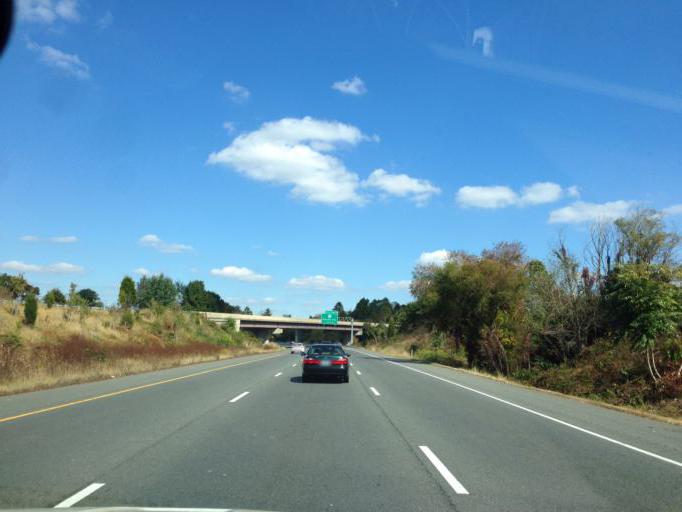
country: US
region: Maryland
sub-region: Howard County
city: Columbia
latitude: 39.2501
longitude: -76.8253
